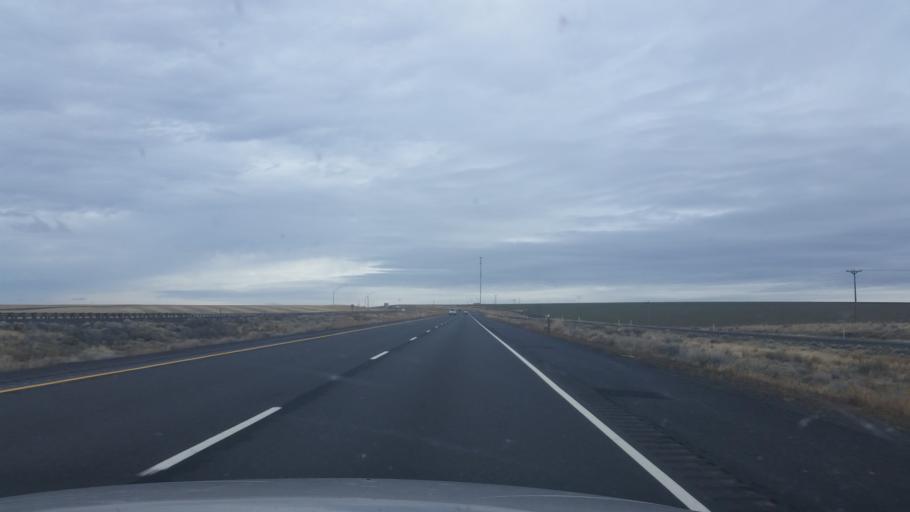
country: US
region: Washington
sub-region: Adams County
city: Ritzville
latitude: 47.0973
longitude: -118.6683
